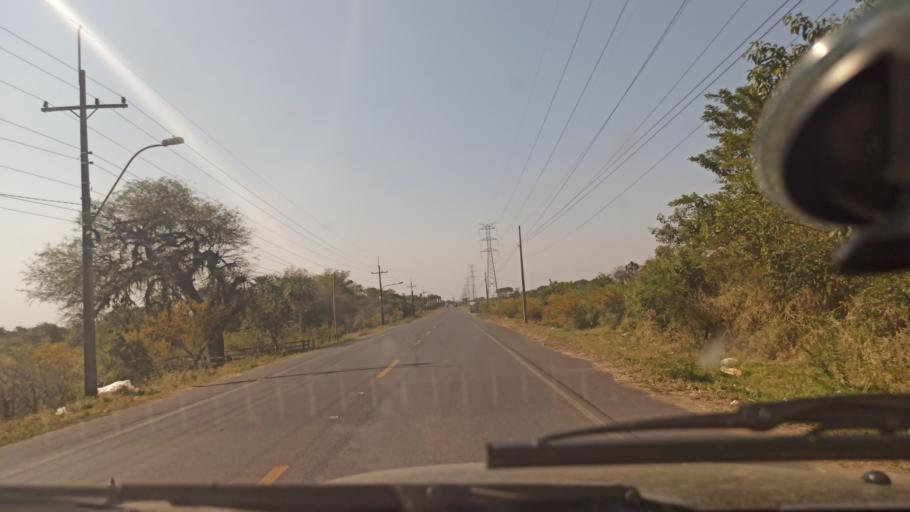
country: PY
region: Presidente Hayes
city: Nanawa
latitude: -25.2638
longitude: -57.6854
